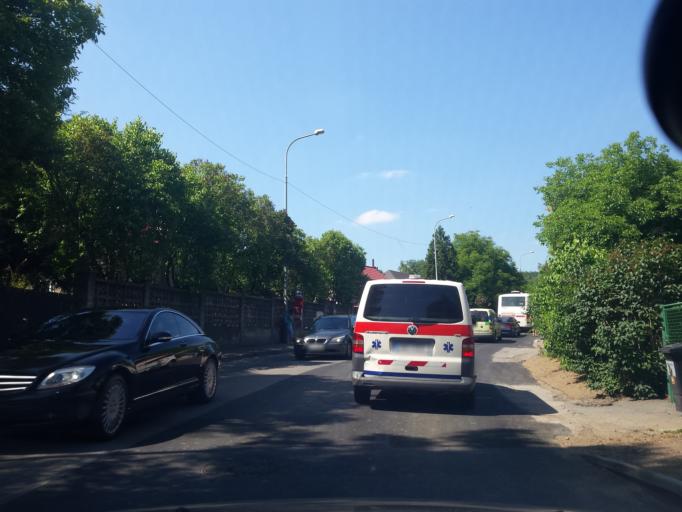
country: CZ
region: Central Bohemia
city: Horomerice
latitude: 50.1062
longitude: 14.3534
